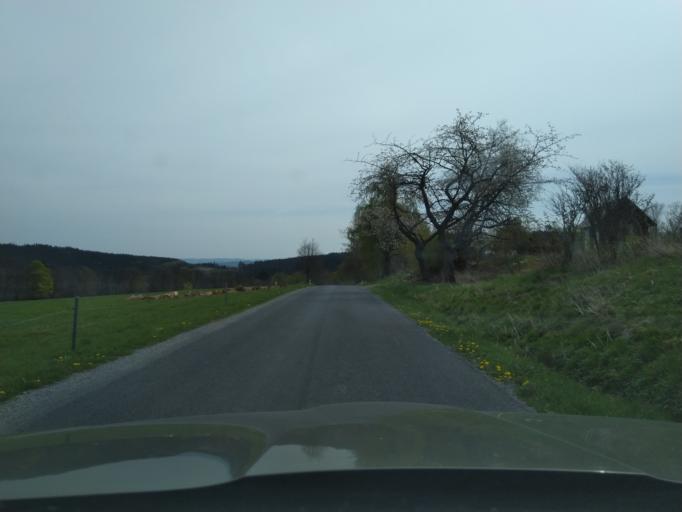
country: CZ
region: Jihocesky
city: Vacov
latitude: 49.1731
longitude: 13.6809
